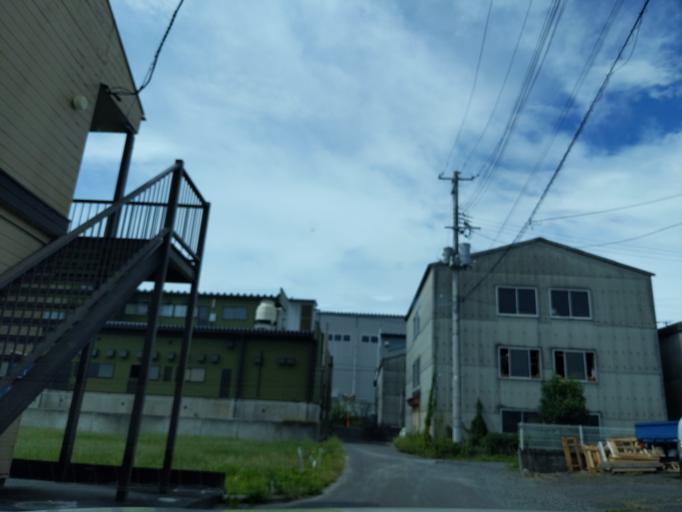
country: JP
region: Fukushima
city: Koriyama
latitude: 37.4059
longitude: 140.3988
